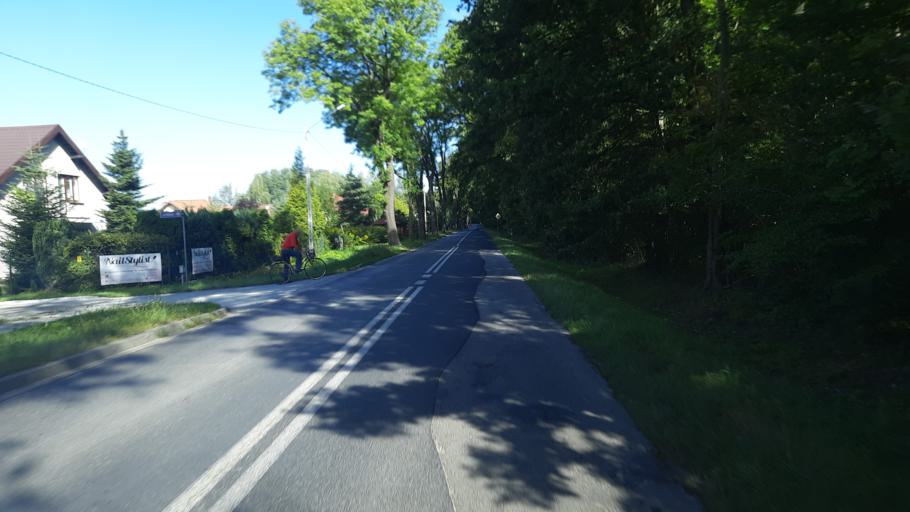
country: PL
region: Lower Silesian Voivodeship
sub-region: Powiat wroclawski
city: Dlugoleka
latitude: 51.1864
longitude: 17.1857
